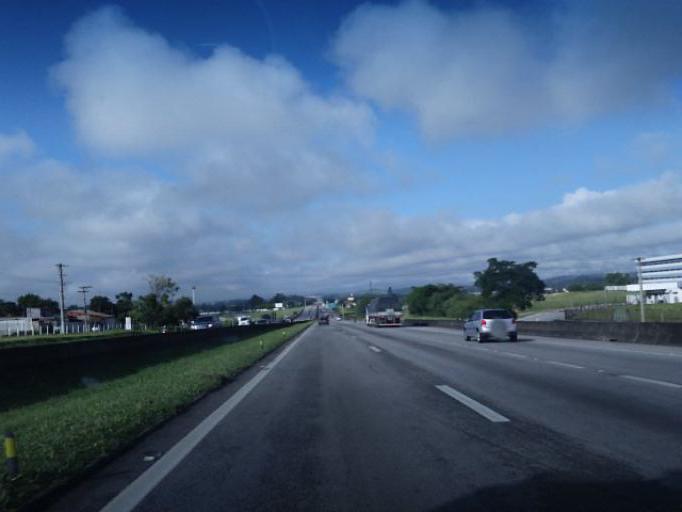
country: BR
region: Sao Paulo
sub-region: Jacarei
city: Jacarei
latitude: -23.2560
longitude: -45.9446
